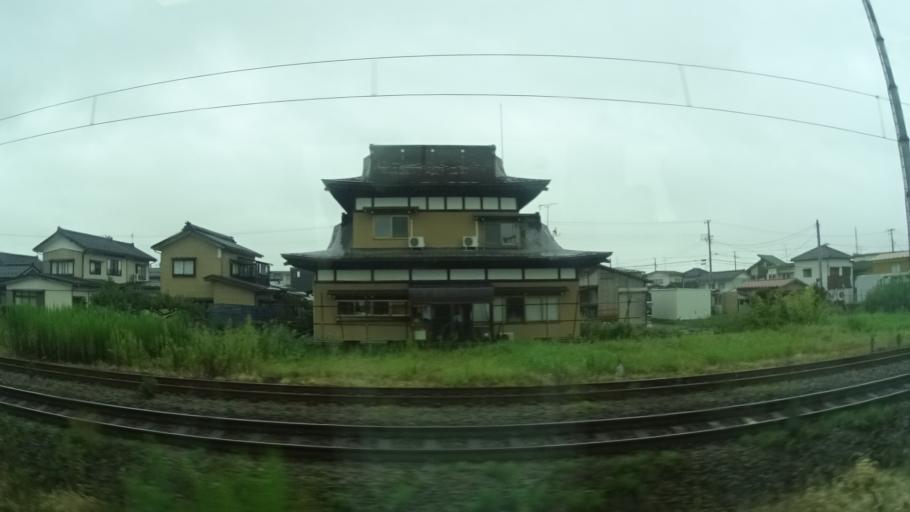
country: JP
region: Yamagata
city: Tsuruoka
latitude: 38.7697
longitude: 139.8954
